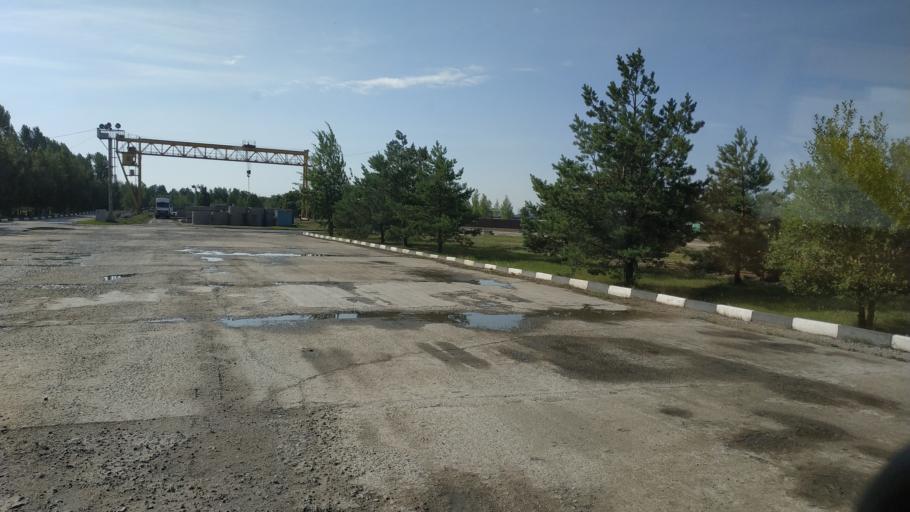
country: BY
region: Mogilev
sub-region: Mahilyowski Rayon
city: Veyno
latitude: 53.8405
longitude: 30.3834
